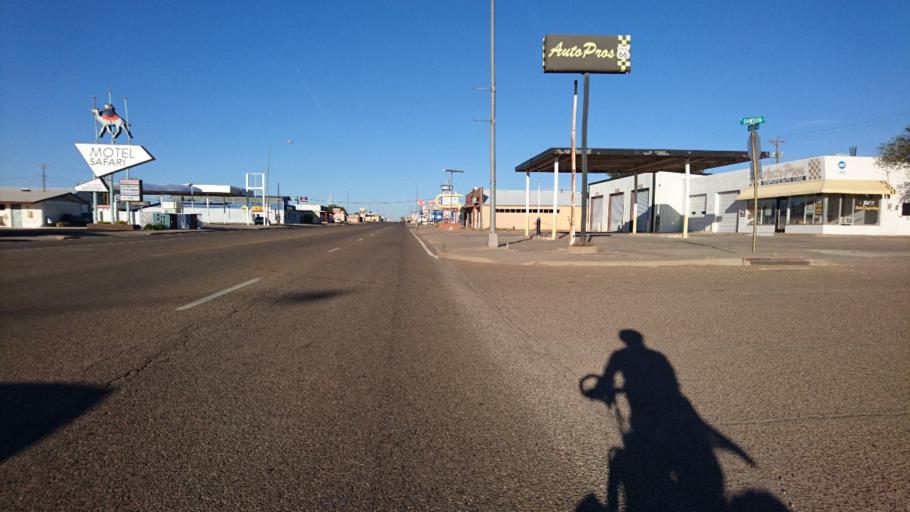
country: US
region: New Mexico
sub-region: Quay County
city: Tucumcari
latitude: 35.1719
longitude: -103.7172
